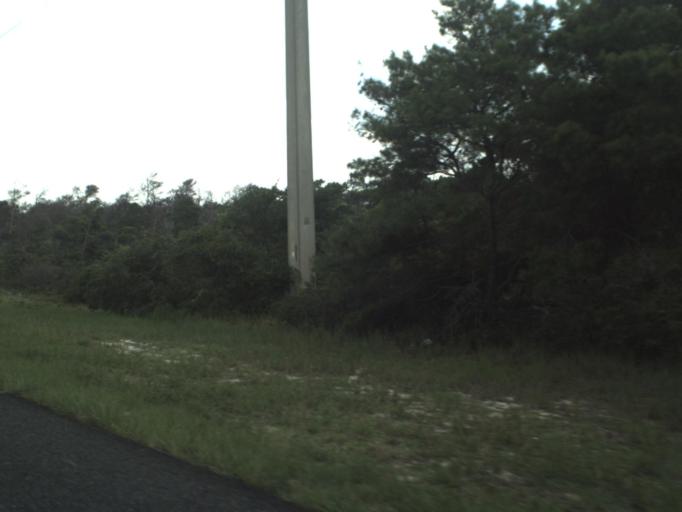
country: US
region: Florida
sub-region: Martin County
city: Hobe Sound
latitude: 27.0301
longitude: -80.1107
